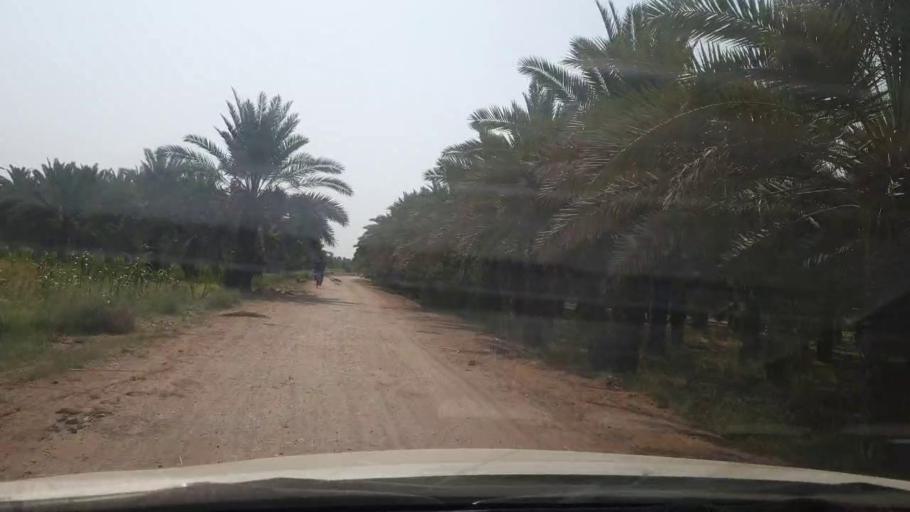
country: PK
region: Sindh
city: Rohri
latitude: 27.5916
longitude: 68.8558
